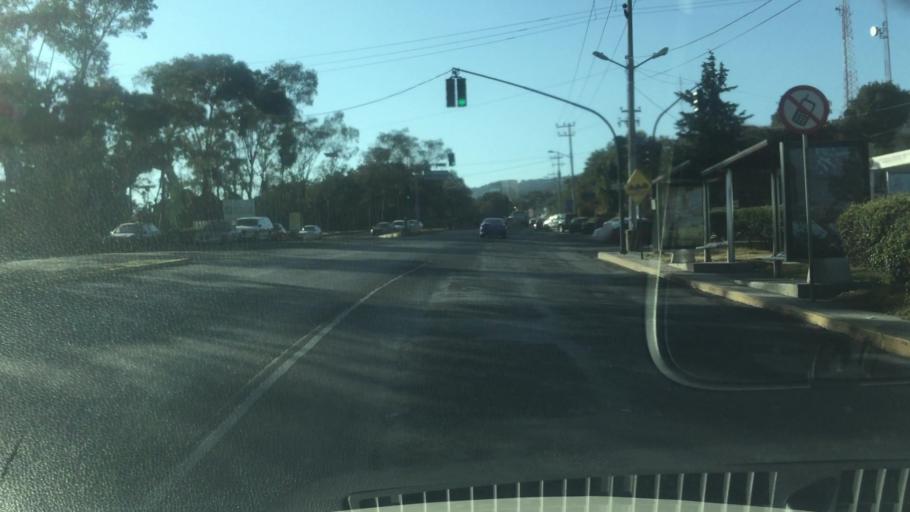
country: MX
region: Mexico City
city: Tlalpan
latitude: 19.2718
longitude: -99.2059
